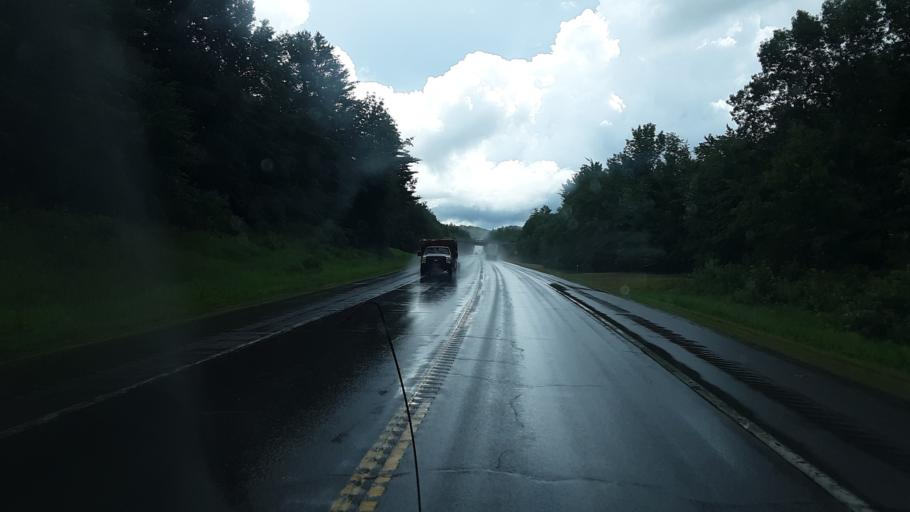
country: US
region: New Hampshire
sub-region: Merrimack County
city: Henniker
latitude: 43.1702
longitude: -71.8518
